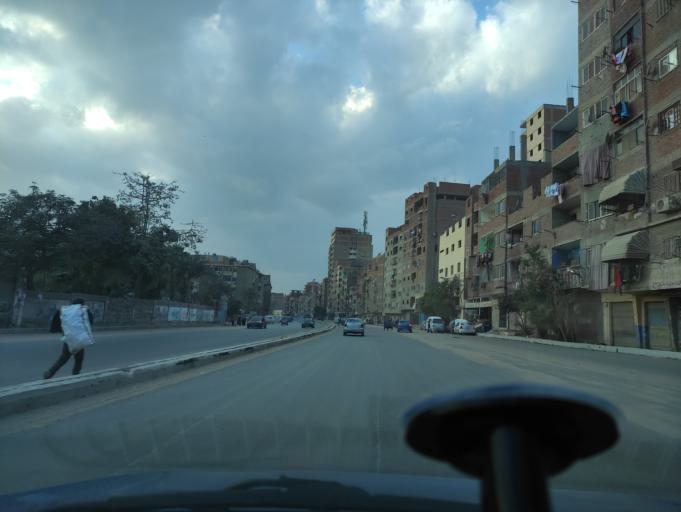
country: EG
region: Muhafazat al Qalyubiyah
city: Al Khankah
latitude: 30.1373
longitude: 31.3495
